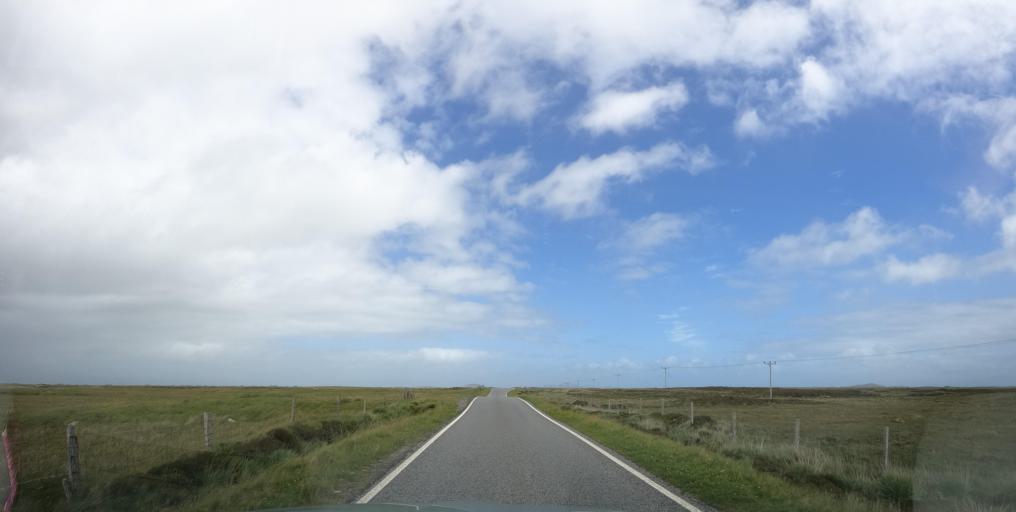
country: GB
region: Scotland
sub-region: Eilean Siar
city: Benbecula
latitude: 57.3676
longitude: -7.3511
